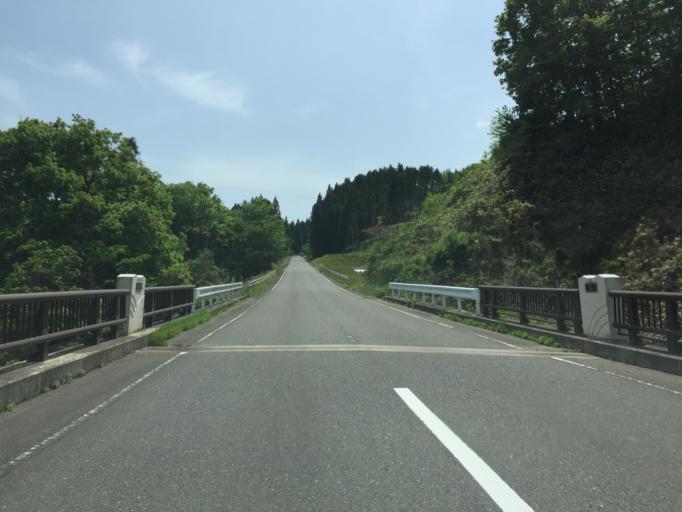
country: JP
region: Fukushima
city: Ishikawa
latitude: 37.1799
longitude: 140.5099
